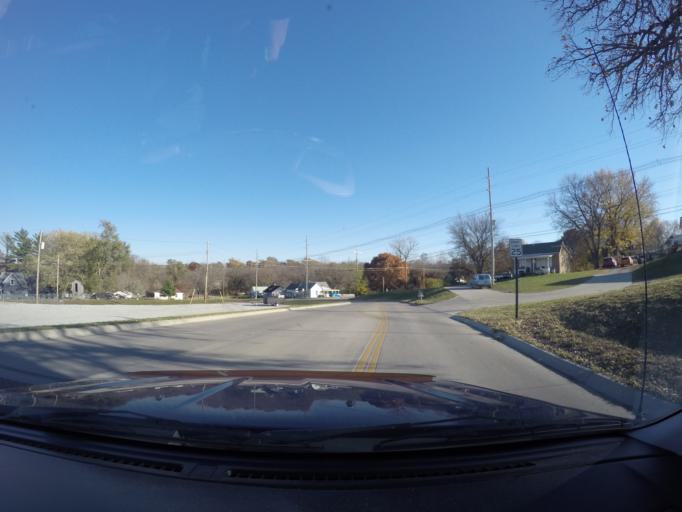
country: US
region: Nebraska
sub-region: Otoe County
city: Nebraska City
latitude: 40.6666
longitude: -95.8590
